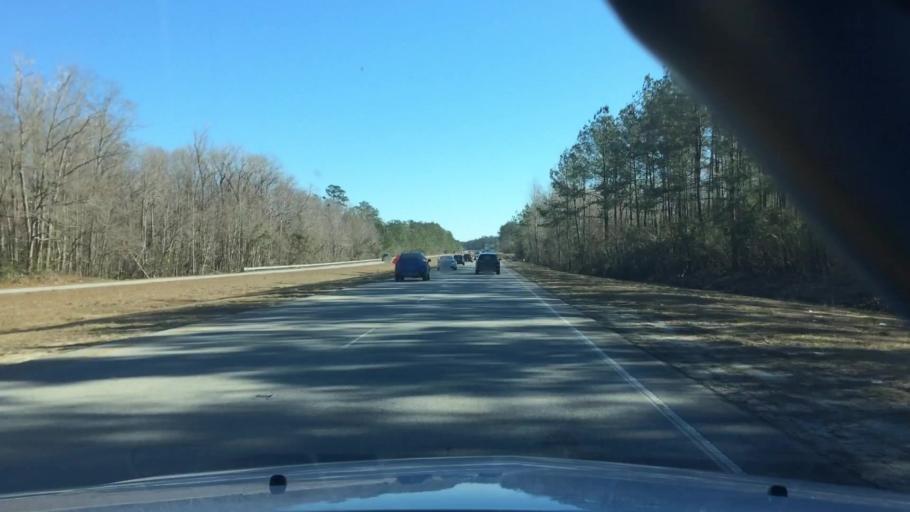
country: US
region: North Carolina
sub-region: Brunswick County
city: Bolivia
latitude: 34.0635
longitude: -78.1958
